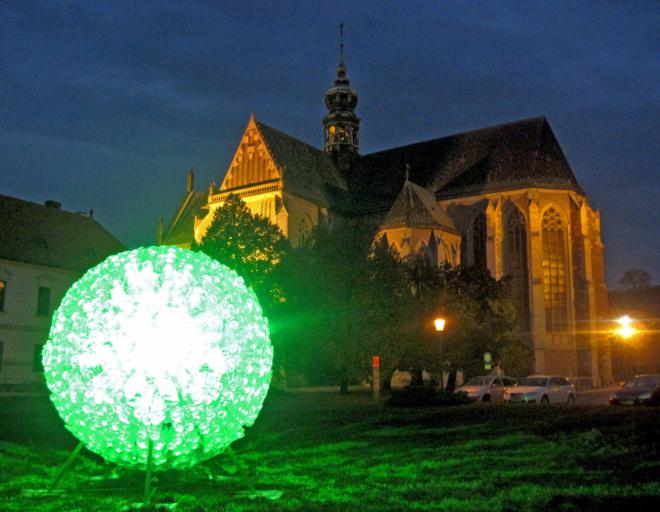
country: CZ
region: South Moravian
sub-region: Mesto Brno
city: Brno
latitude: 49.1912
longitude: 16.5953
